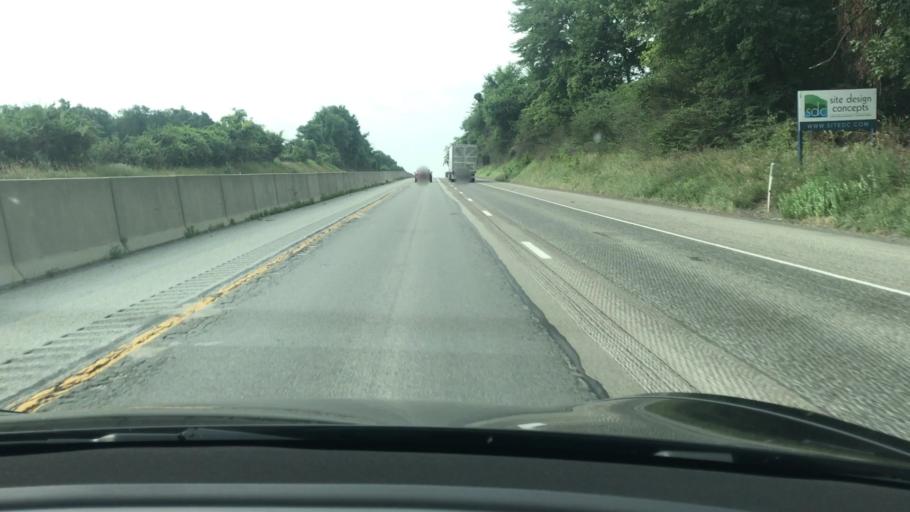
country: US
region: Pennsylvania
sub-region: York County
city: Loganville
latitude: 39.8213
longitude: -76.6831
